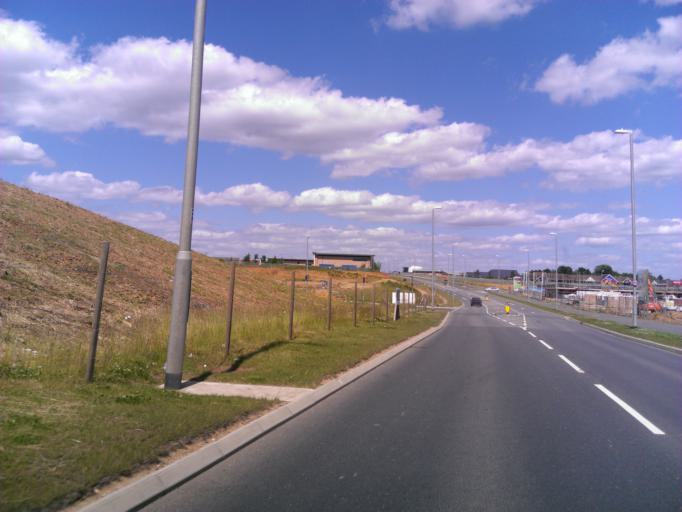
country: GB
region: England
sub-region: Essex
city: Eight Ash Green
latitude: 51.8798
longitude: 0.8270
